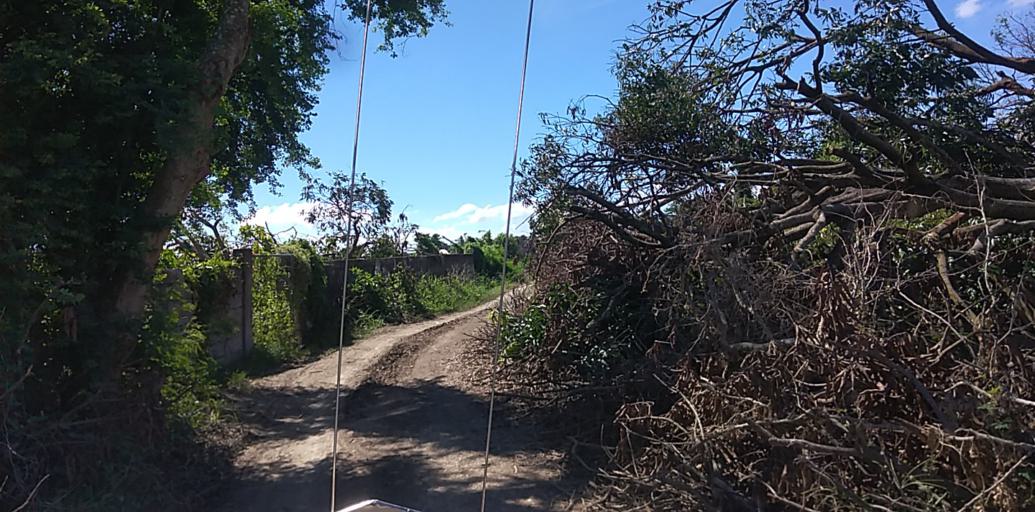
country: PH
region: Central Luzon
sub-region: Province of Pampanga
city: Arayat
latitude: 15.1292
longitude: 120.7935
